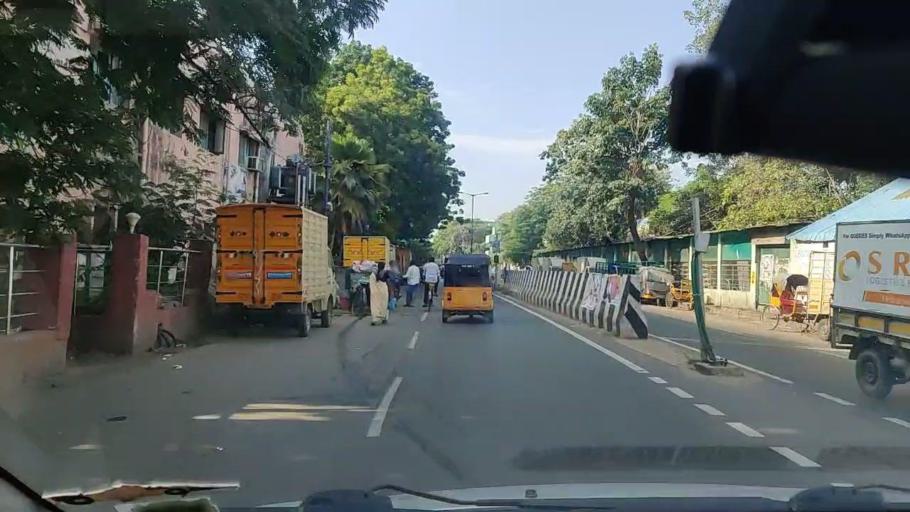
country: IN
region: Tamil Nadu
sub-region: Chennai
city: George Town
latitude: 13.0975
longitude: 80.2752
